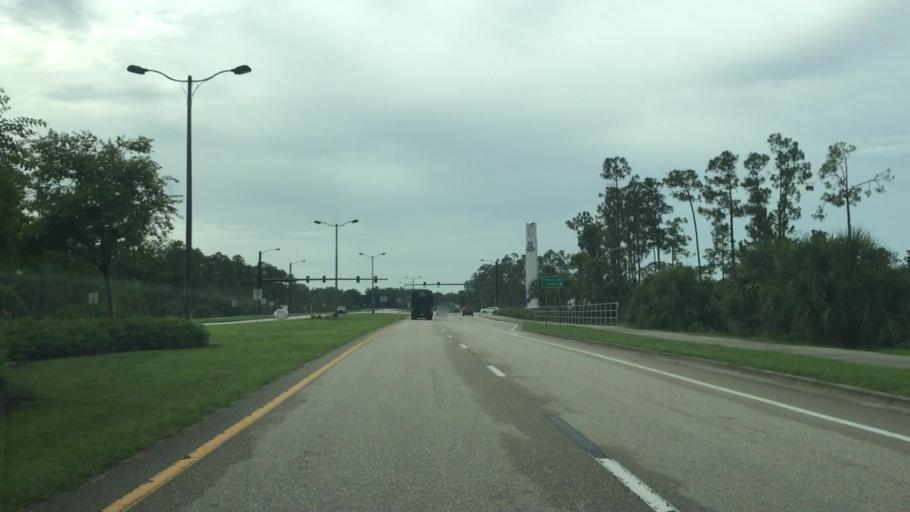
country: US
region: Florida
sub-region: Lee County
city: Three Oaks
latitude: 26.4600
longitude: -81.7833
